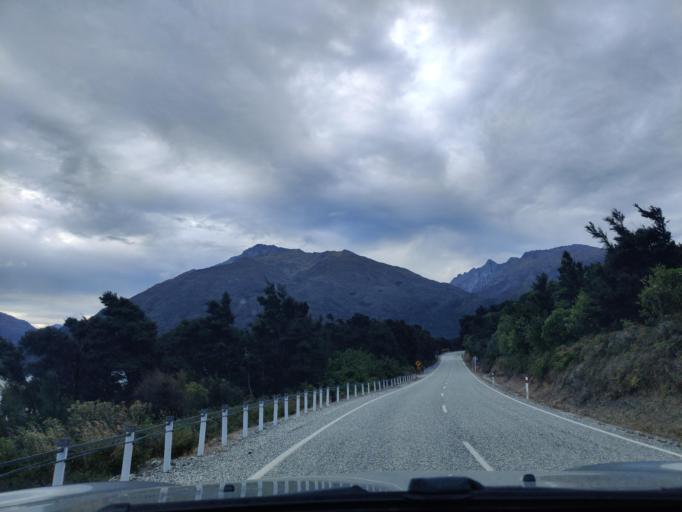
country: NZ
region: Otago
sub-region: Queenstown-Lakes District
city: Wanaka
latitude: -44.3561
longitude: 169.1722
